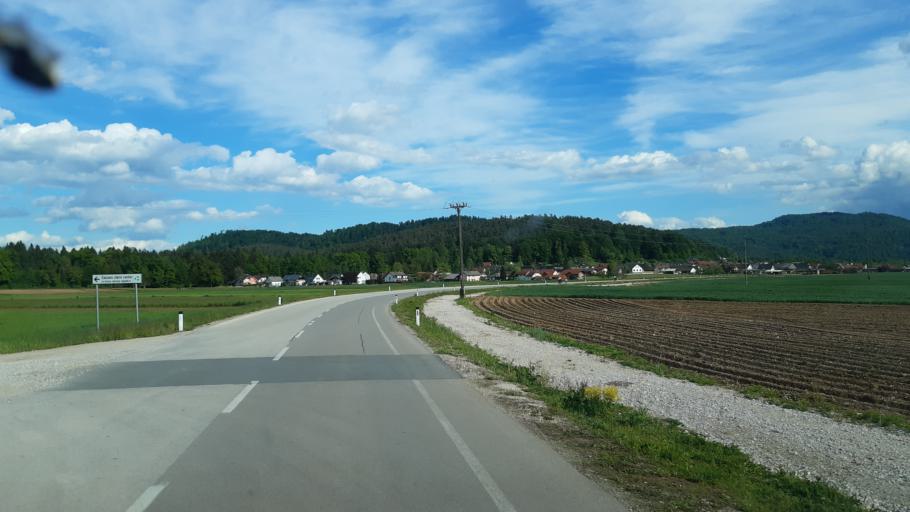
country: SI
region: Vodice
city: Vodice
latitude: 46.1820
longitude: 14.5009
